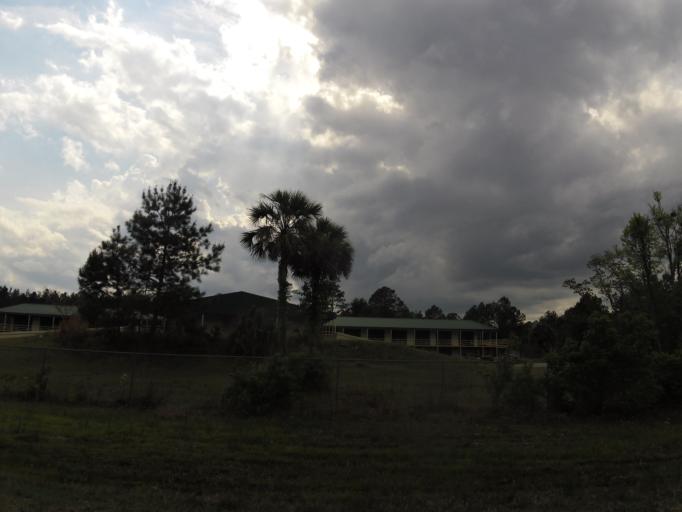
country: US
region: Georgia
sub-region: Charlton County
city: Folkston
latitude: 30.8659
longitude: -82.0126
